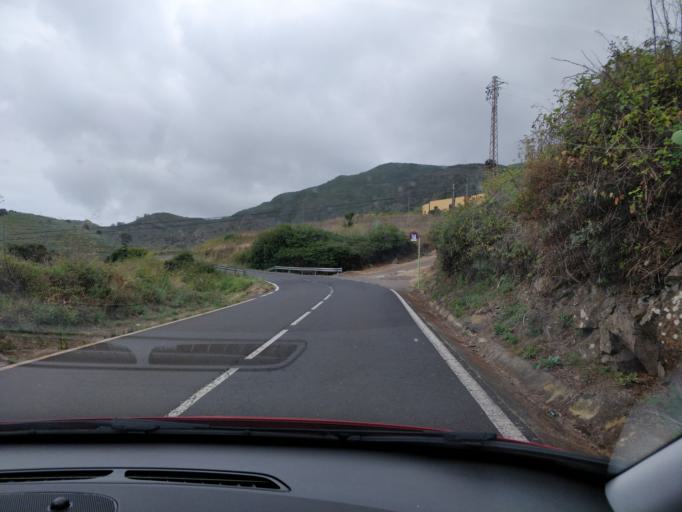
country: ES
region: Canary Islands
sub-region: Provincia de Santa Cruz de Tenerife
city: Tanque
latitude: 28.3345
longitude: -16.8496
